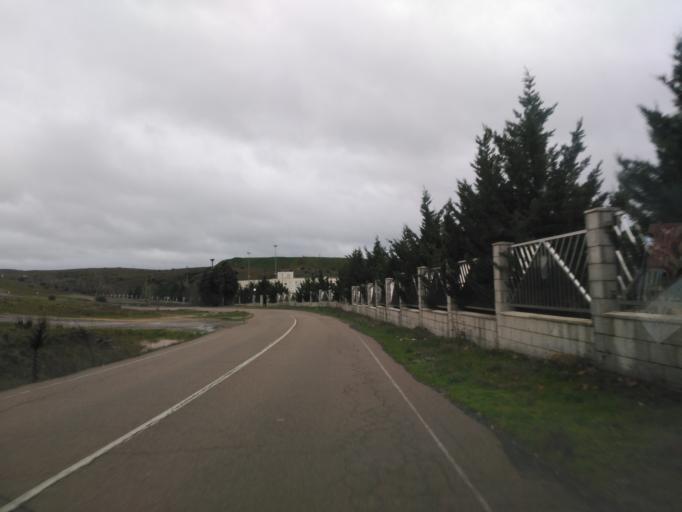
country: ES
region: Castille and Leon
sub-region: Provincia de Salamanca
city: Doninos de Salamanca
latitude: 40.9720
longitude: -5.7137
